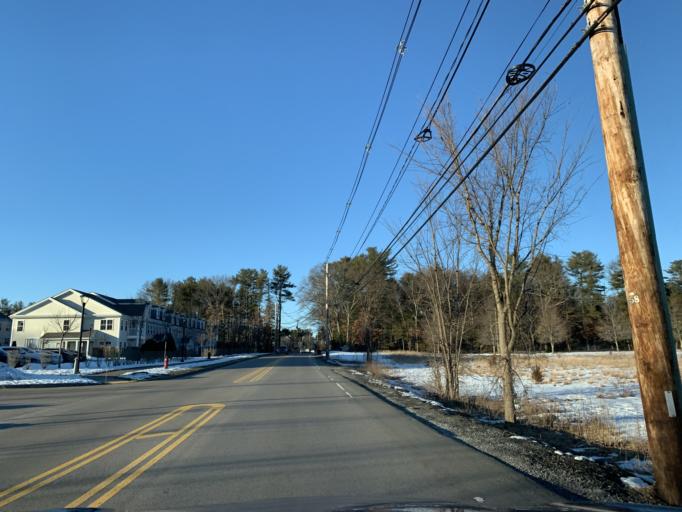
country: US
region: Massachusetts
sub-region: Bristol County
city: Norton Center
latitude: 41.9898
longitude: -71.1553
